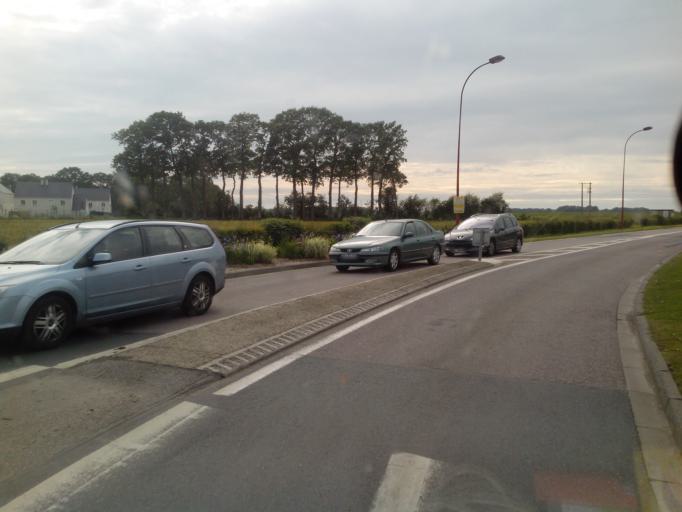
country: FR
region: Haute-Normandie
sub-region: Departement de la Seine-Maritime
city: Fauville-en-Caux
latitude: 49.6593
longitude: 0.5926
